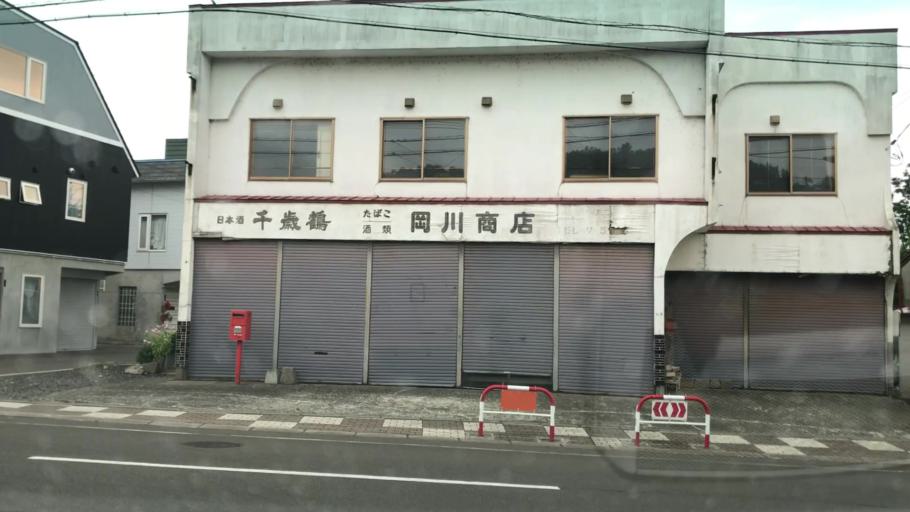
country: JP
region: Hokkaido
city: Niseko Town
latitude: 42.8033
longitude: 140.5263
